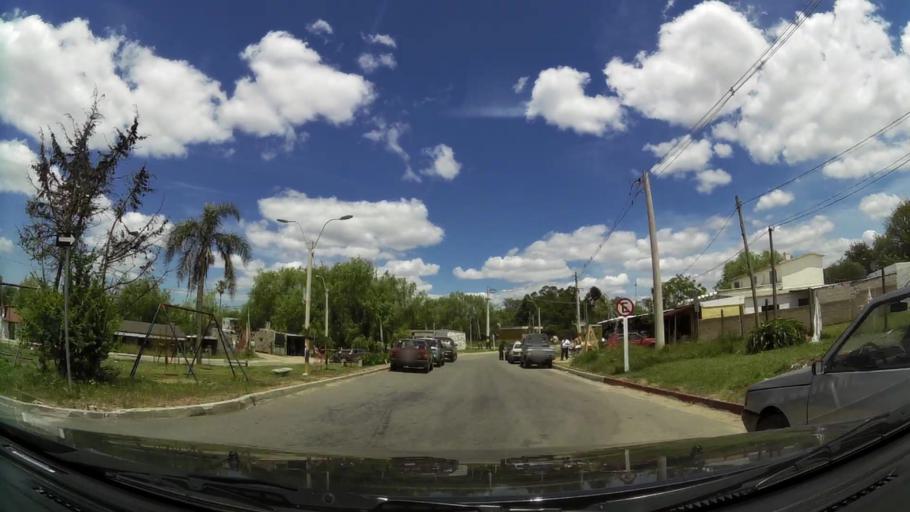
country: UY
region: Canelones
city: Colonia Nicolich
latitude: -34.8197
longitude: -56.0053
